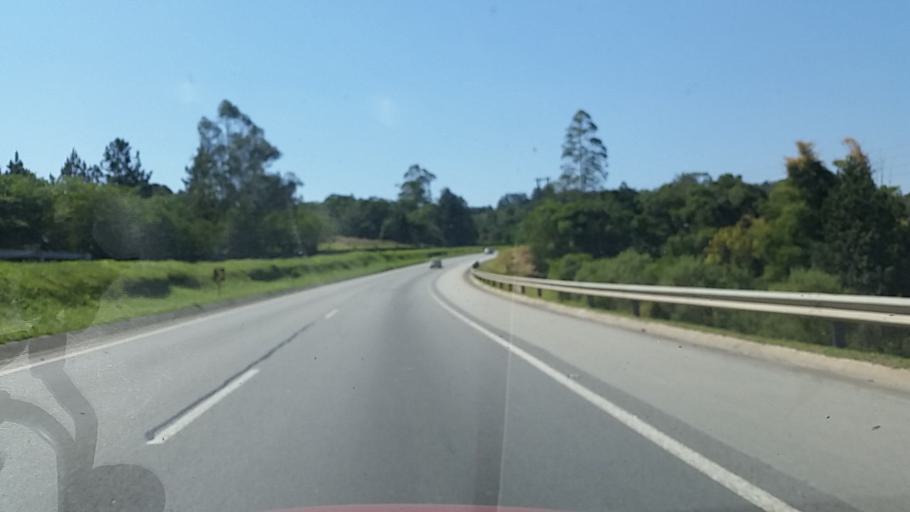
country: BR
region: Sao Paulo
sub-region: Juquitiba
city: Juquitiba
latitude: -23.9683
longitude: -47.1327
